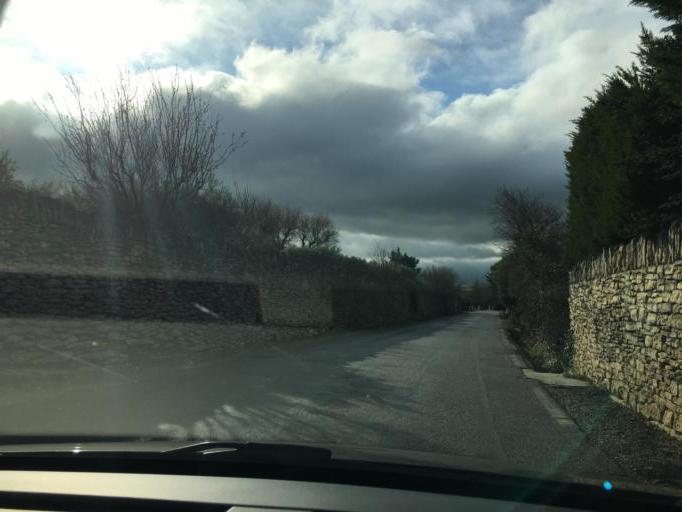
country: FR
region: Provence-Alpes-Cote d'Azur
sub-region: Departement du Vaucluse
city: Gordes
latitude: 43.9059
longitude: 5.1974
